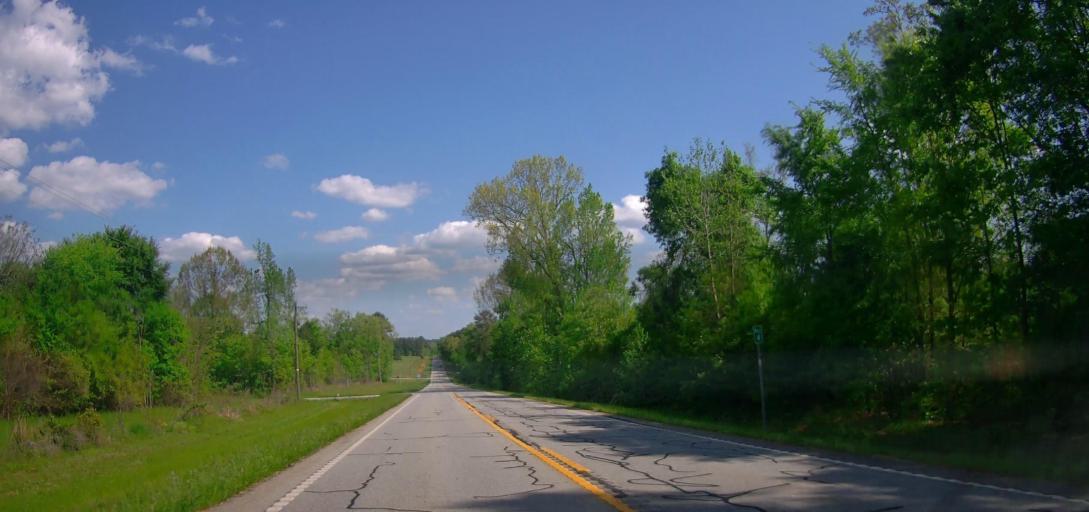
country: US
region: Georgia
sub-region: Greene County
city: Greensboro
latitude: 33.5946
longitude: -83.2919
